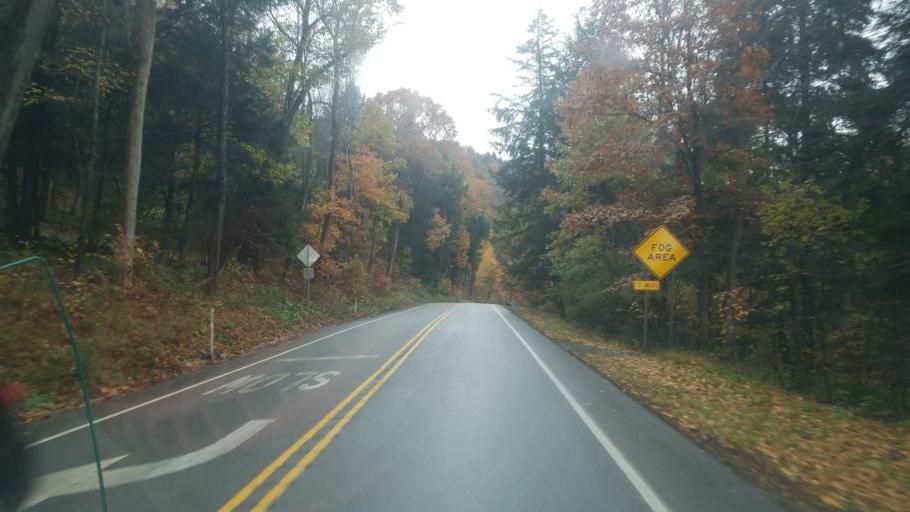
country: US
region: Pennsylvania
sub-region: Clearfield County
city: Clearfield
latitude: 41.0545
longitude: -78.3775
